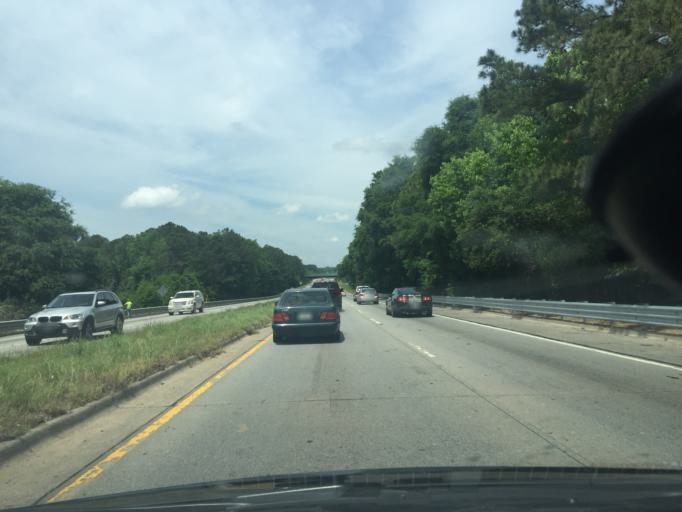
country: US
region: Georgia
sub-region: Chatham County
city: Savannah
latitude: 32.0360
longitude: -81.1358
